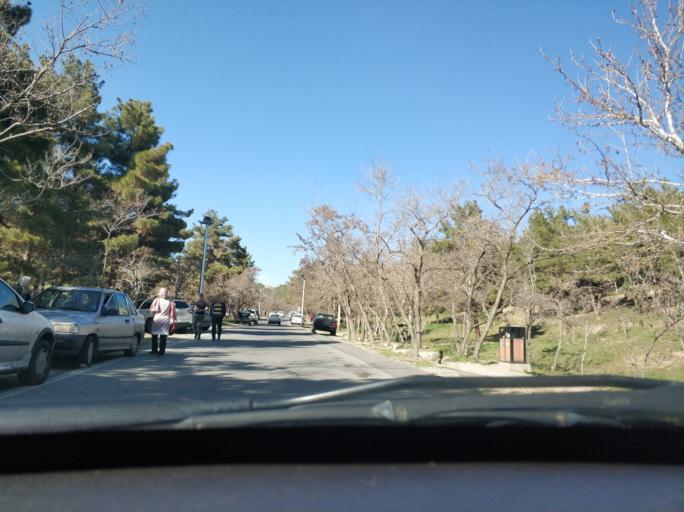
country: IR
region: Tehran
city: Tajrish
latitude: 35.7858
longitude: 51.5584
